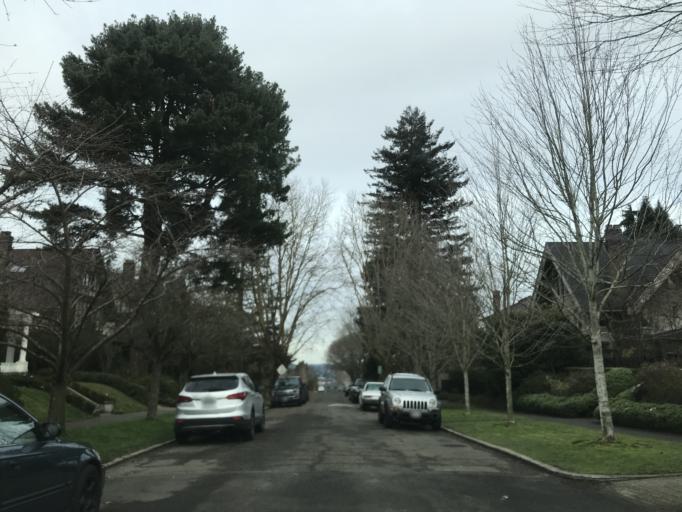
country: US
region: Washington
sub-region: King County
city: Seattle
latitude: 47.6298
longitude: -122.3047
